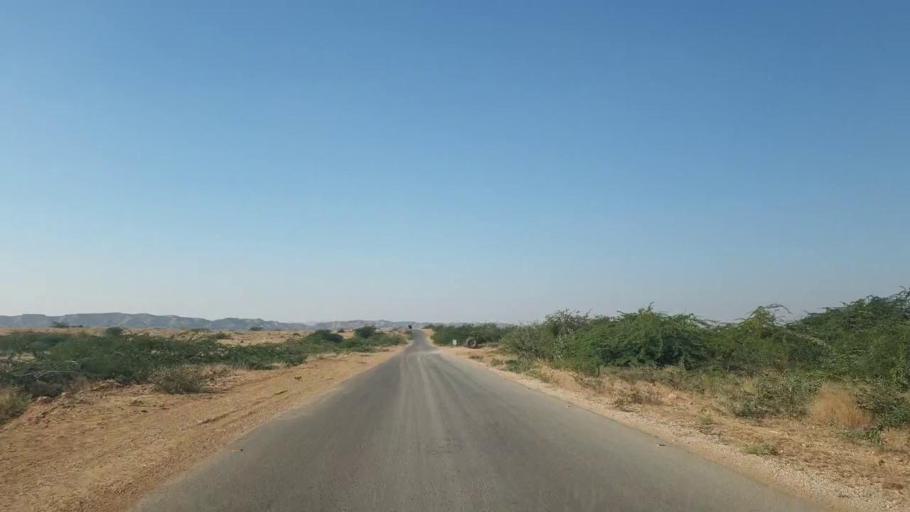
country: PK
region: Sindh
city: Malir Cantonment
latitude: 25.2802
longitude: 67.5845
